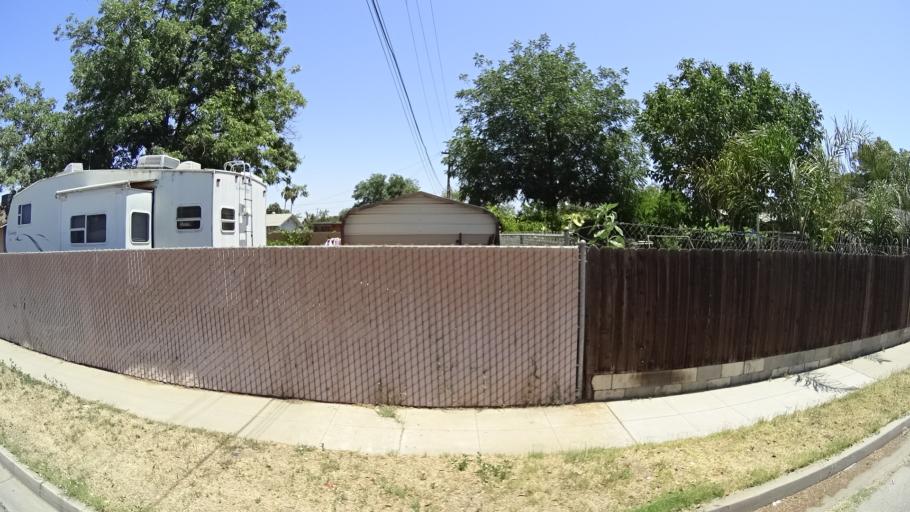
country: US
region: California
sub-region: Fresno County
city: West Park
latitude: 36.7226
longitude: -119.8267
